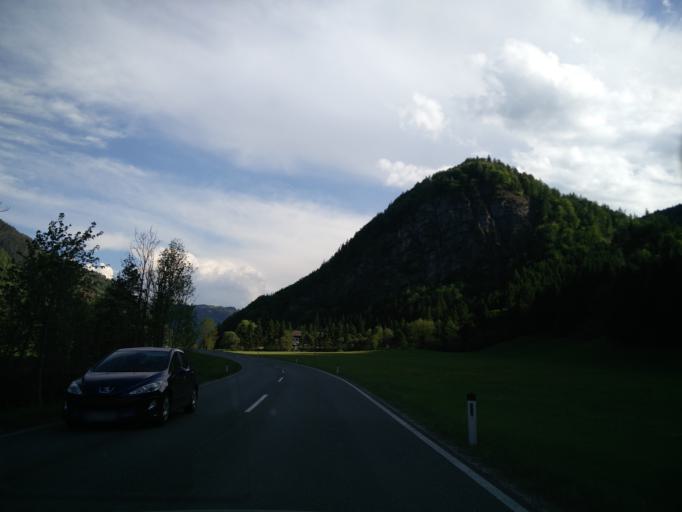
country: DE
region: Bavaria
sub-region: Upper Bavaria
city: Reit im Winkl
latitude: 47.6168
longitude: 12.4645
